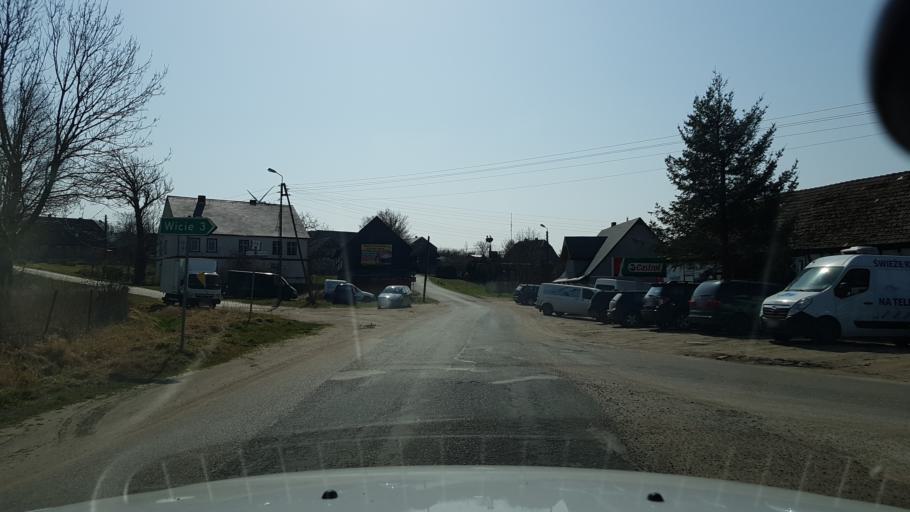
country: PL
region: West Pomeranian Voivodeship
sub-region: Powiat slawienski
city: Darlowo
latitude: 54.4815
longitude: 16.5081
